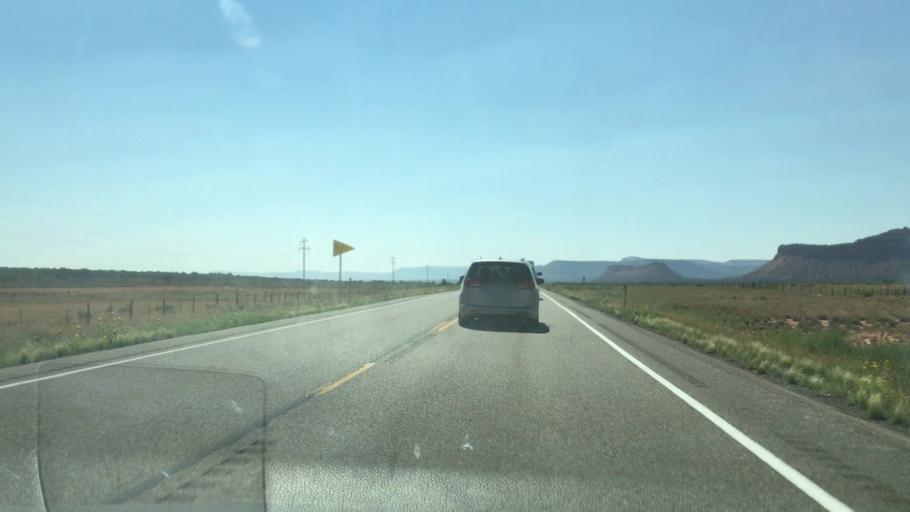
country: US
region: Utah
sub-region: Kane County
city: Kanab
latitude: 37.0395
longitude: -112.2818
